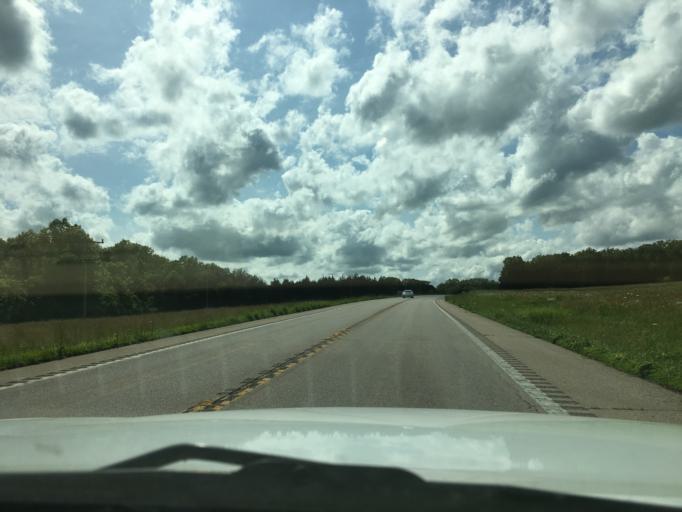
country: US
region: Missouri
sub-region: Franklin County
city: Gerald
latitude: 38.4203
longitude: -91.2545
